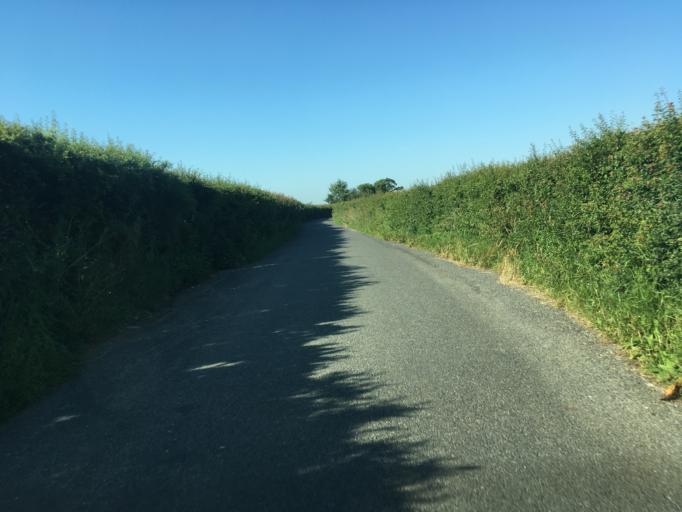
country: GB
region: England
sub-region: South Gloucestershire
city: Hinton
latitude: 51.4773
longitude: -2.3921
